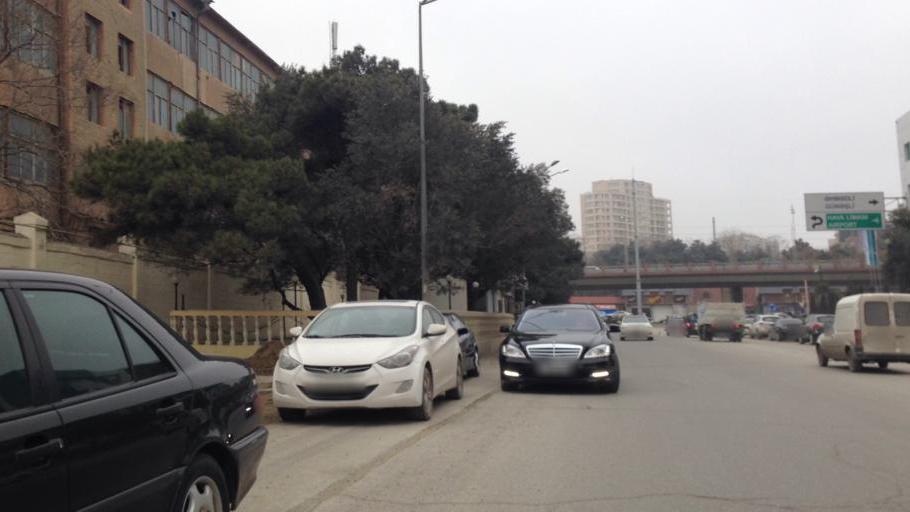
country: AZ
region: Baki
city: Baku
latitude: 40.3876
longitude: 49.8761
